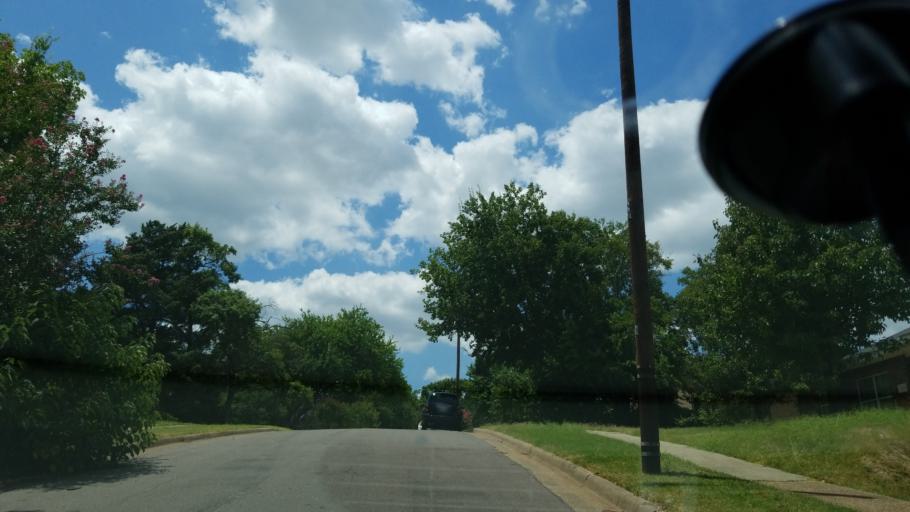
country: US
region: Texas
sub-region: Dallas County
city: Cockrell Hill
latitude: 32.6985
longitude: -96.8504
